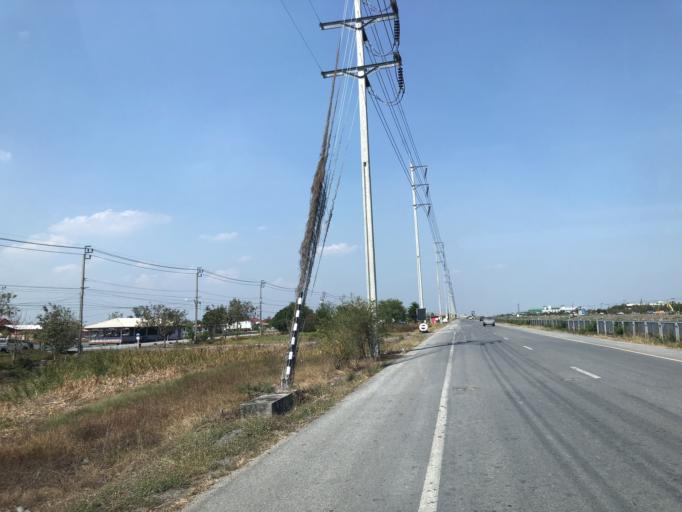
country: TH
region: Samut Prakan
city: Bang Bo District
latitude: 13.5099
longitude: 100.7448
